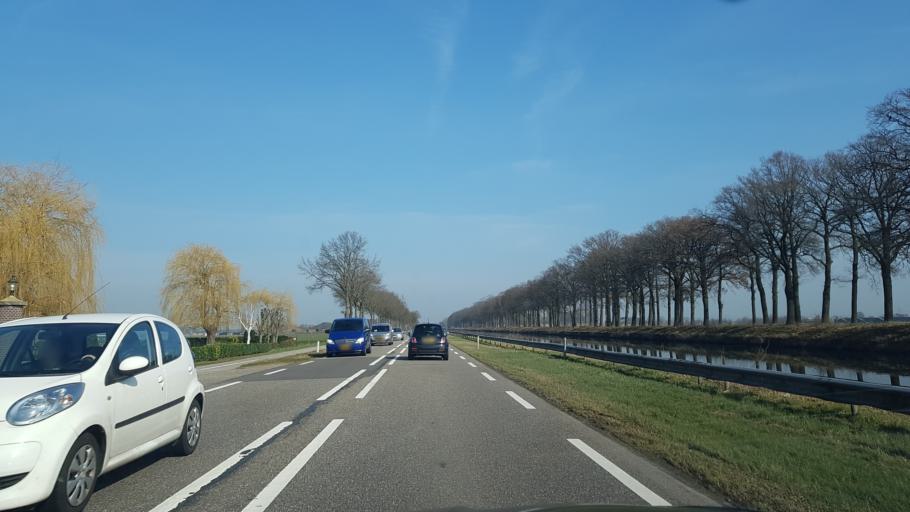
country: NL
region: Limburg
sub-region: Gemeente Nederweert
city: Nederweert
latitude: 51.3109
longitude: 5.7497
